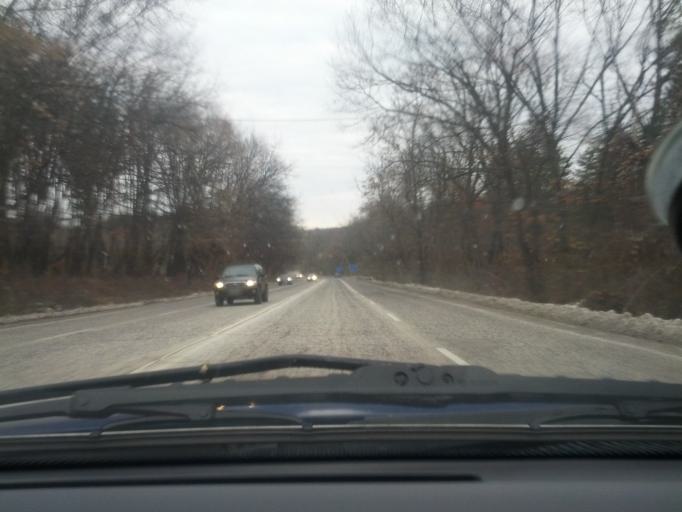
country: BG
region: Vratsa
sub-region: Obshtina Vratsa
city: Vratsa
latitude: 43.2662
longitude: 23.6055
